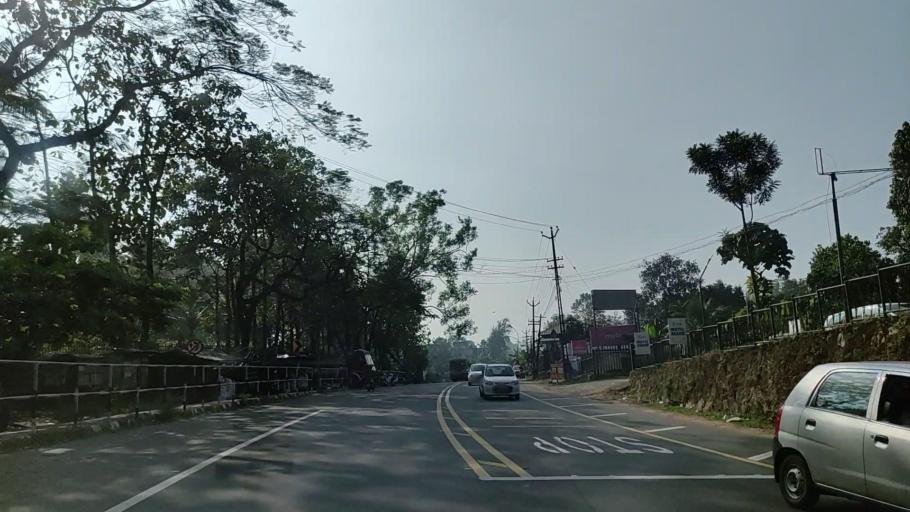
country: IN
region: Kerala
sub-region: Kollam
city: Punalur
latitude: 8.9813
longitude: 76.8101
